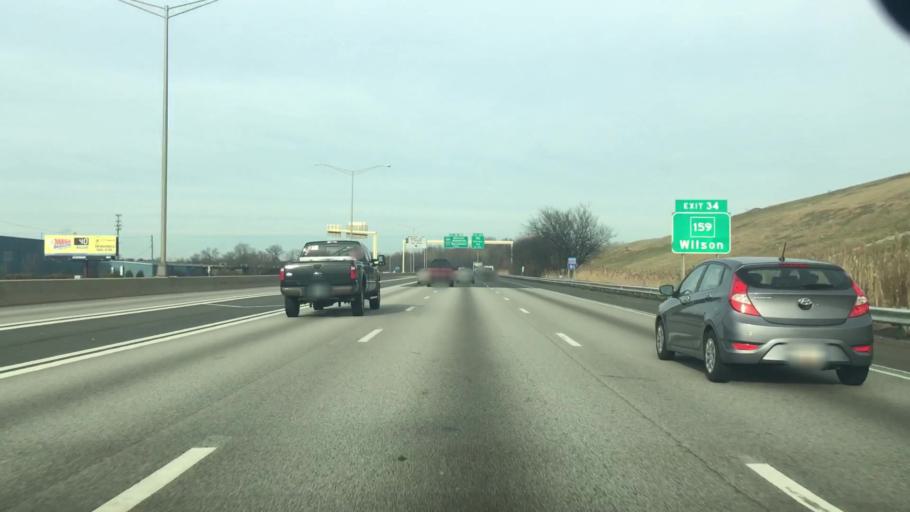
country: US
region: Connecticut
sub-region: Hartford County
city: Hartford
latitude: 41.7934
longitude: -72.6542
